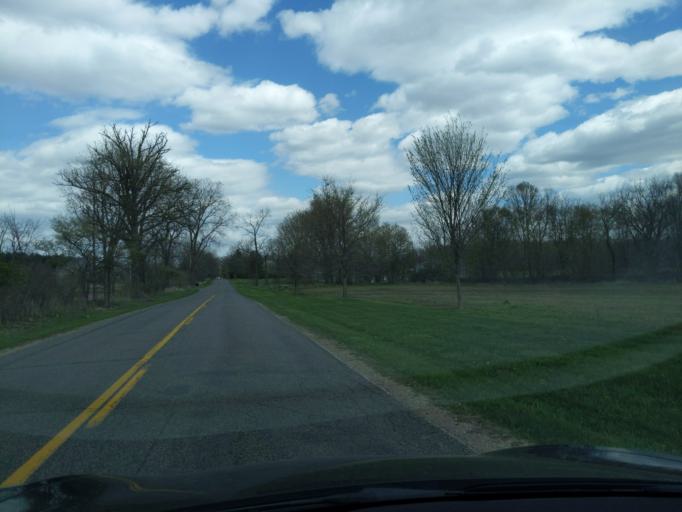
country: US
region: Michigan
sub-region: Ingham County
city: Holt
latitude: 42.6258
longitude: -84.5741
